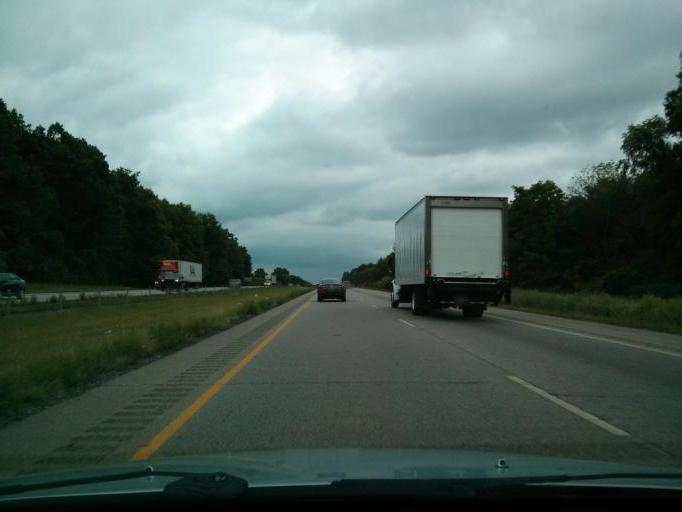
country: US
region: Ohio
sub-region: Portage County
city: Ravenna
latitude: 41.1059
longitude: -81.1398
